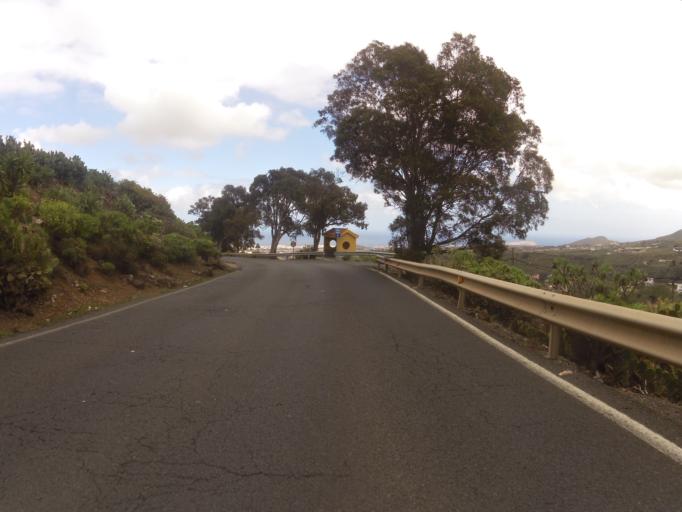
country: ES
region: Canary Islands
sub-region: Provincia de Las Palmas
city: Telde
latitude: 27.9938
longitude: -15.4566
